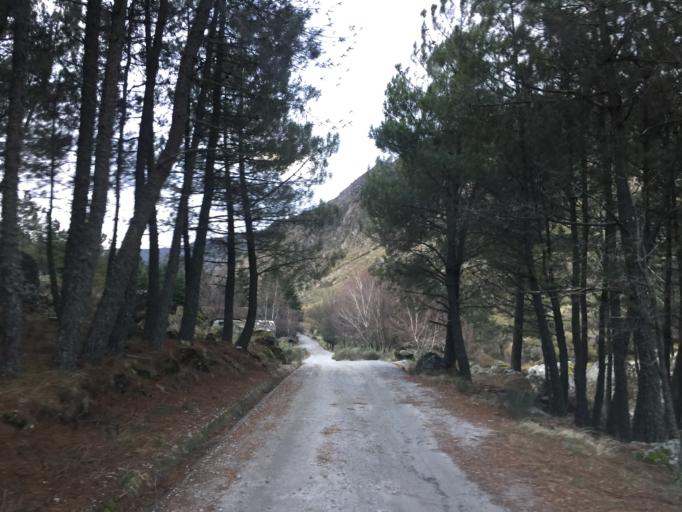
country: PT
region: Guarda
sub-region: Manteigas
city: Manteigas
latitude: 40.3577
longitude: -7.5568
